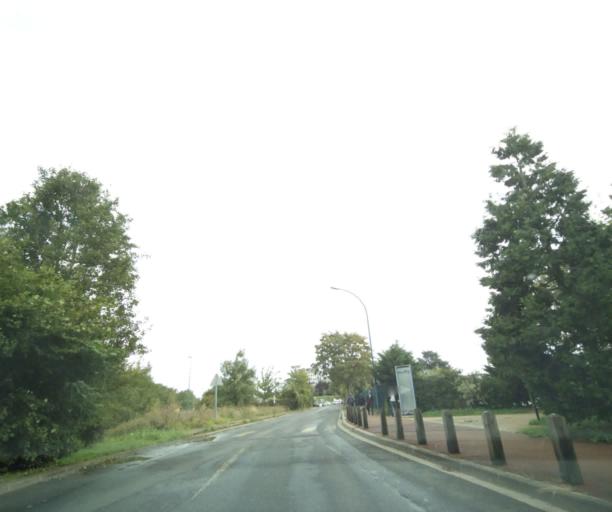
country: FR
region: Ile-de-France
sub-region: Departement des Hauts-de-Seine
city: Le Plessis-Robinson
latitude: 48.7846
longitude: 2.2537
